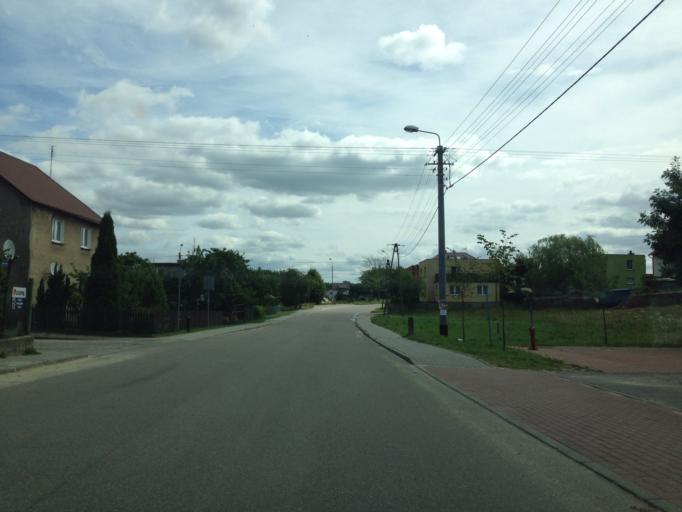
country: PL
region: Pomeranian Voivodeship
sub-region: Powiat koscierski
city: Lipusz
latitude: 54.0988
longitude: 17.7878
